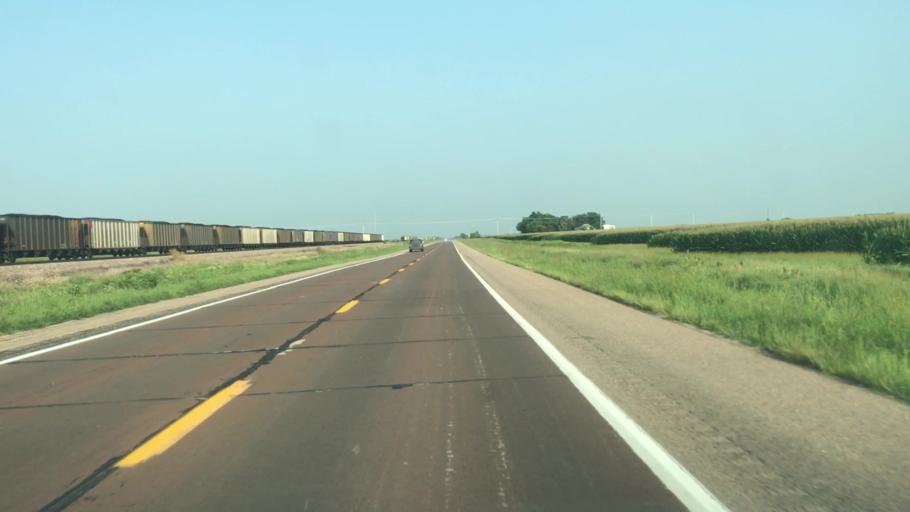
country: US
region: Nebraska
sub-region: Hall County
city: Wood River
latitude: 40.9995
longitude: -98.5954
